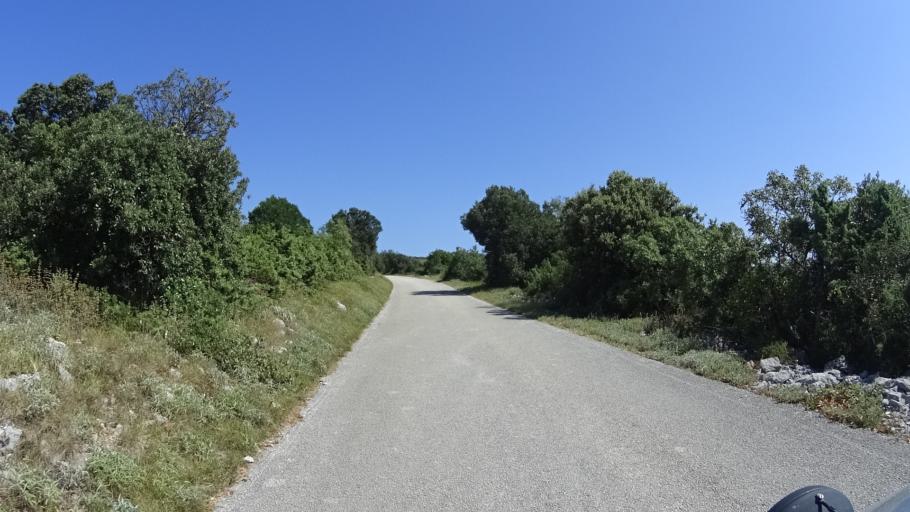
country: HR
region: Istarska
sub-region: Grad Labin
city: Rabac
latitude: 44.9748
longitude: 14.1485
